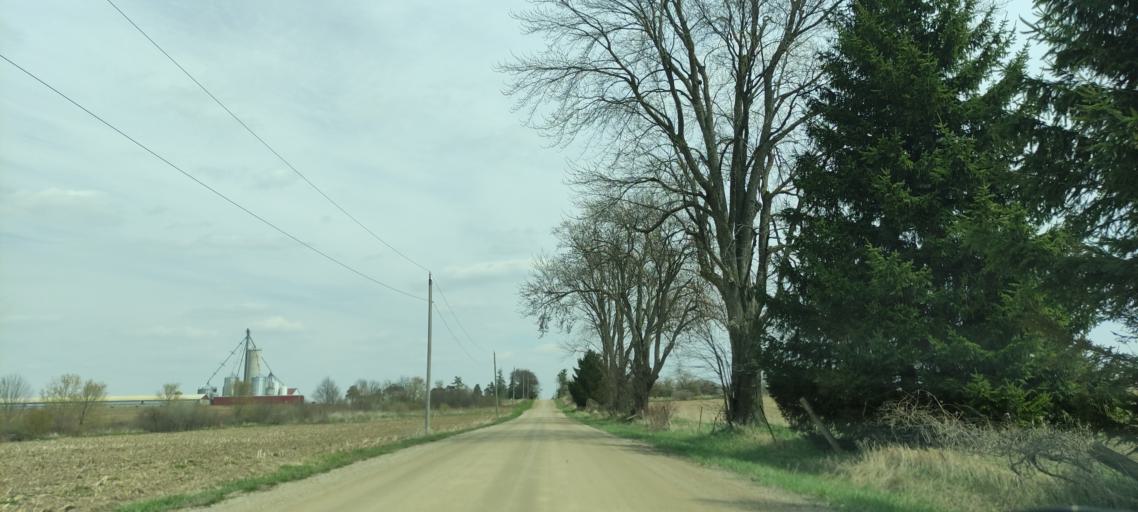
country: CA
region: Ontario
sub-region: Oxford County
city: Woodstock
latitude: 43.2785
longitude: -80.6937
